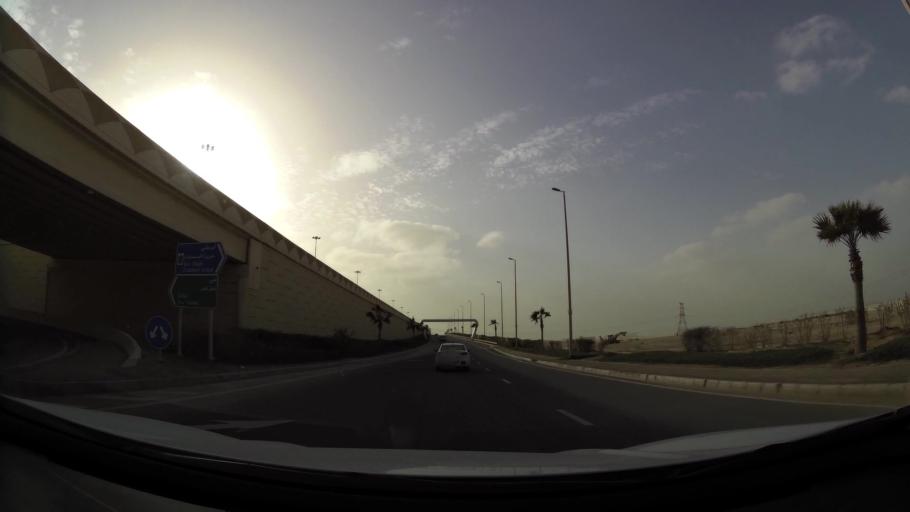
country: AE
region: Abu Dhabi
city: Abu Dhabi
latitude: 24.5028
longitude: 54.5800
